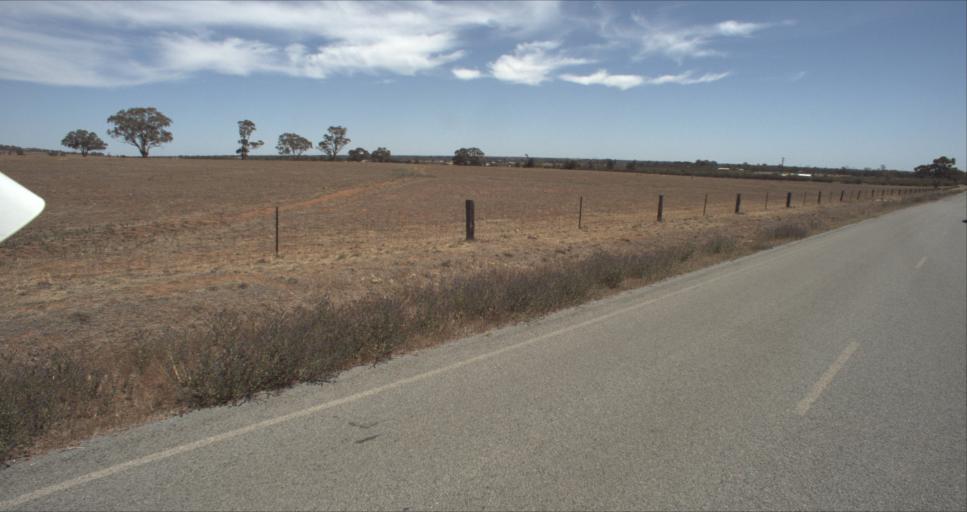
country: AU
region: New South Wales
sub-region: Leeton
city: Leeton
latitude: -34.5891
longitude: 146.4463
